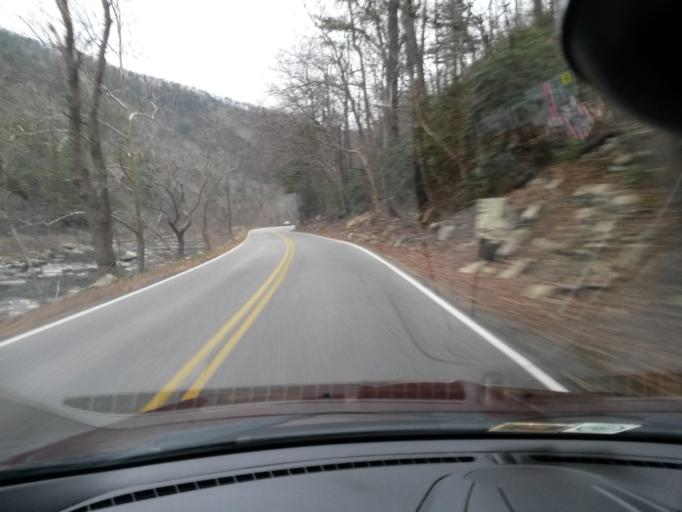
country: US
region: Virginia
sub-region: Rockbridge County
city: East Lexington
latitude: 37.9435
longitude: -79.4554
